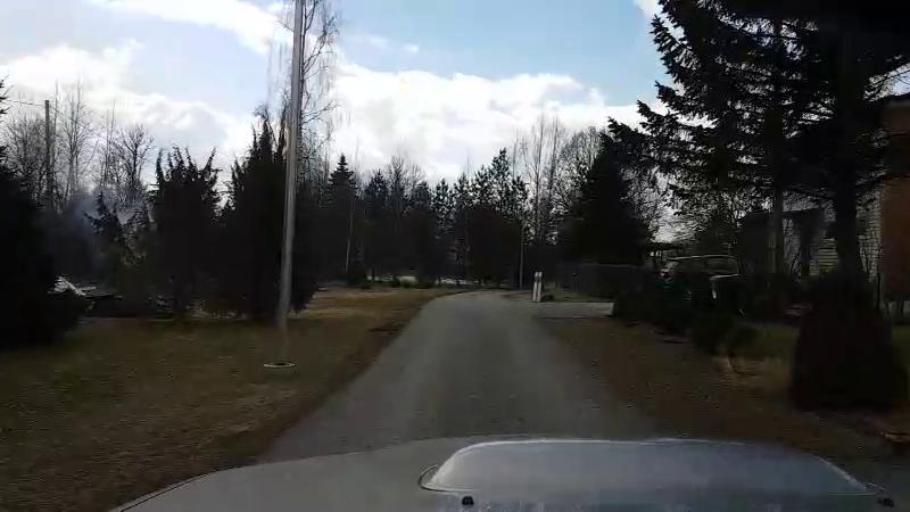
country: EE
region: Jaervamaa
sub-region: Paide linn
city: Paide
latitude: 58.8870
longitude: 25.5787
